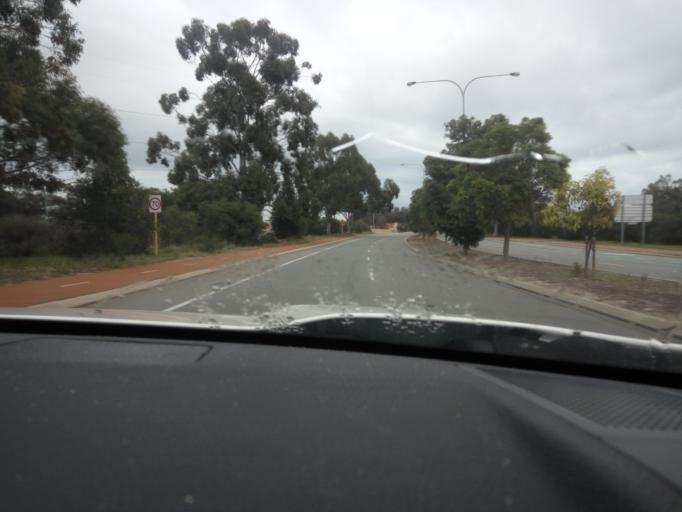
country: AU
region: Western Australia
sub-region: City of Cockburn
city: City of Cockburn
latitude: -32.1107
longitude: 115.8486
